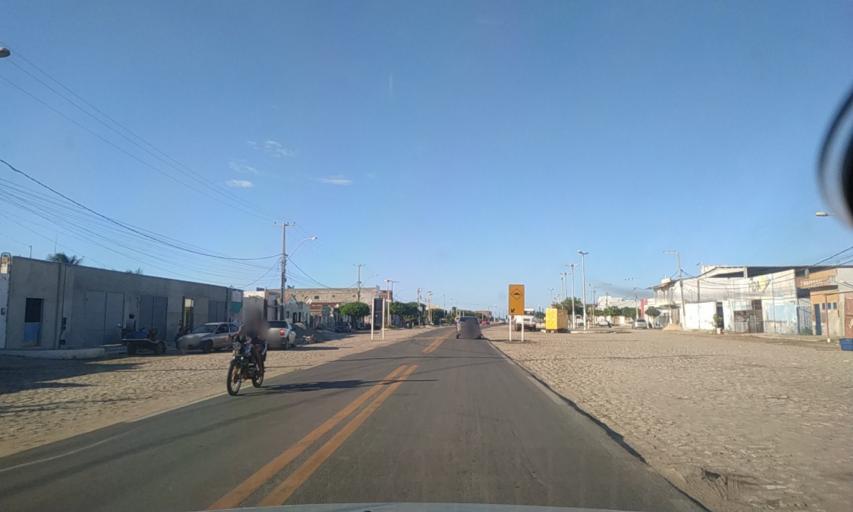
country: BR
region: Rio Grande do Norte
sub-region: Areia Branca
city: Areia Branca
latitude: -4.9520
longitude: -37.1275
